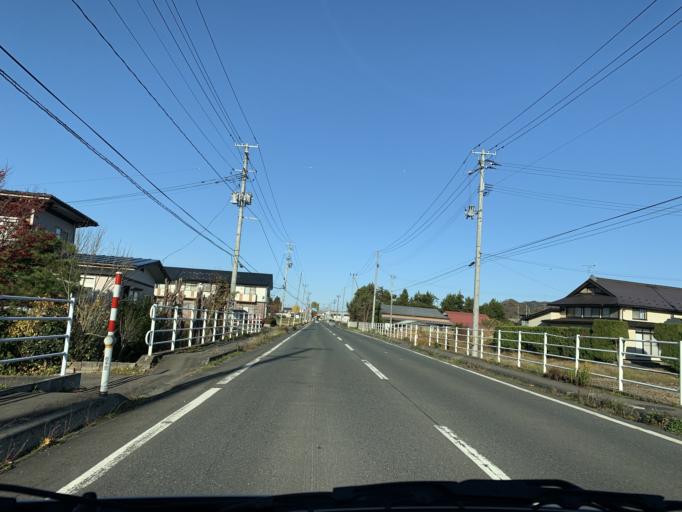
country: JP
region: Iwate
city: Kitakami
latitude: 39.2527
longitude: 141.1083
